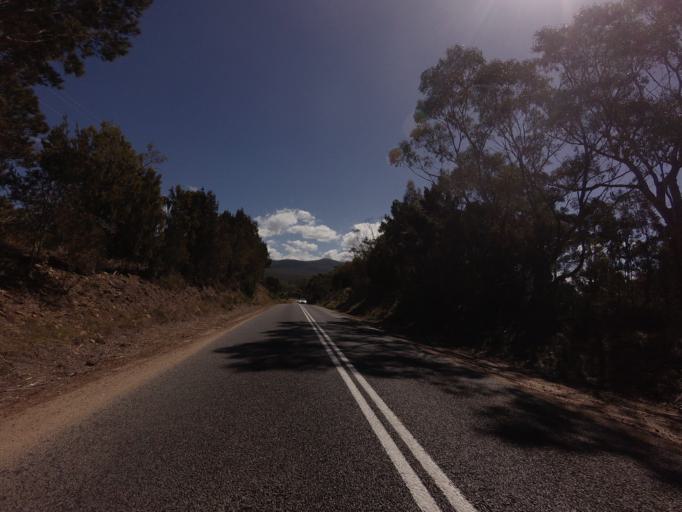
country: AU
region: Tasmania
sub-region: Break O'Day
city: St Helens
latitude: -41.7848
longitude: 148.2597
